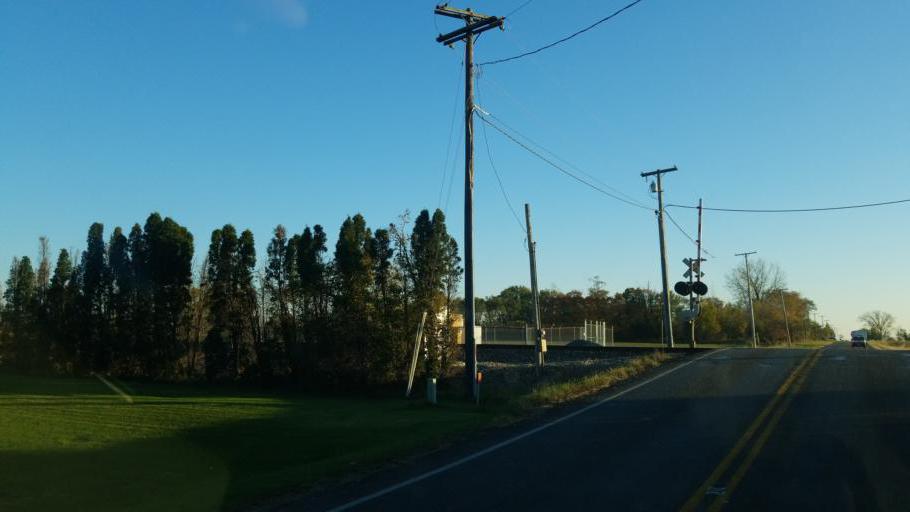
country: US
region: Ohio
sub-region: Sandusky County
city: Mount Carmel
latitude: 41.2636
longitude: -82.9752
